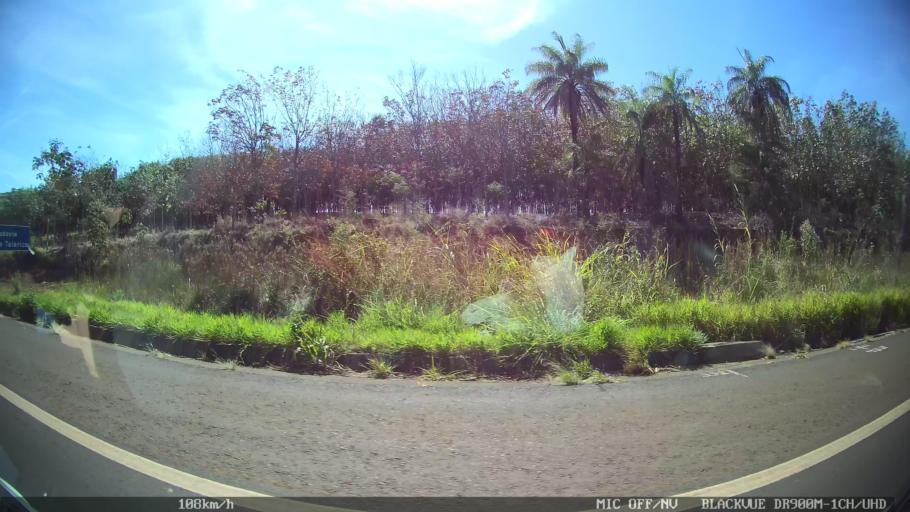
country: BR
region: Sao Paulo
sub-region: Franca
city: Franca
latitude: -20.5596
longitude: -47.5355
